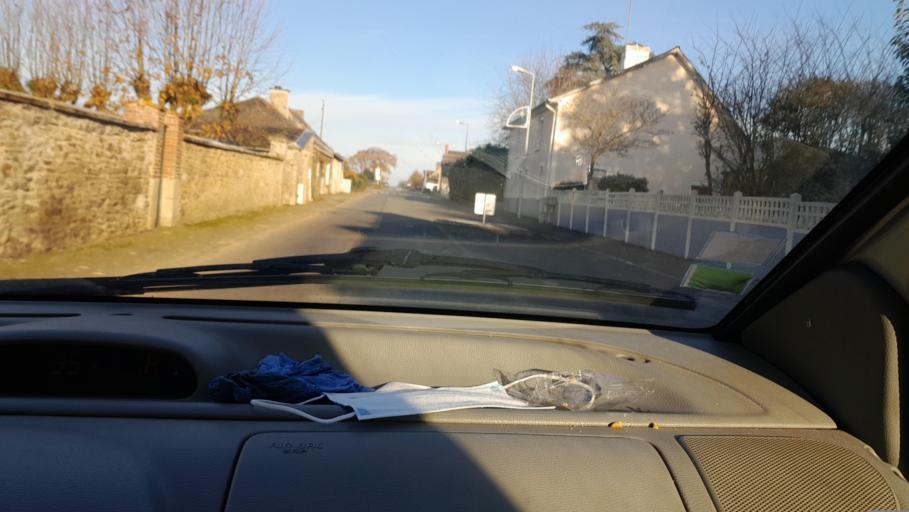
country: FR
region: Brittany
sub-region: Departement d'Ille-et-Vilaine
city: Rannee
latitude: 47.8870
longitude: -1.1818
